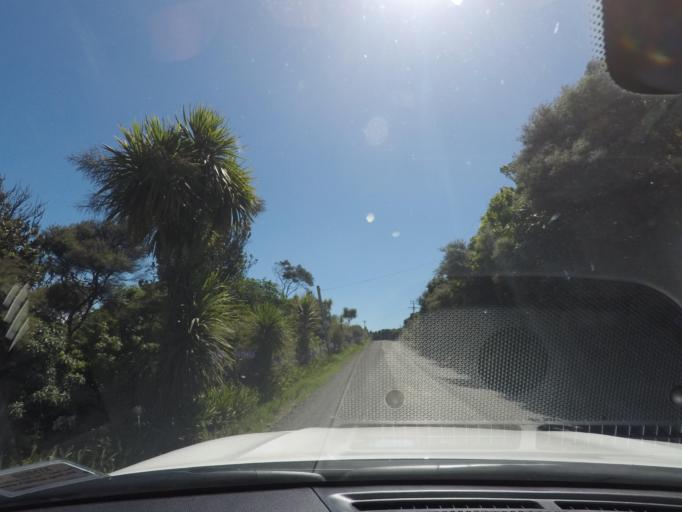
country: NZ
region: Auckland
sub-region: Auckland
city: Parakai
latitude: -36.5832
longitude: 174.3072
